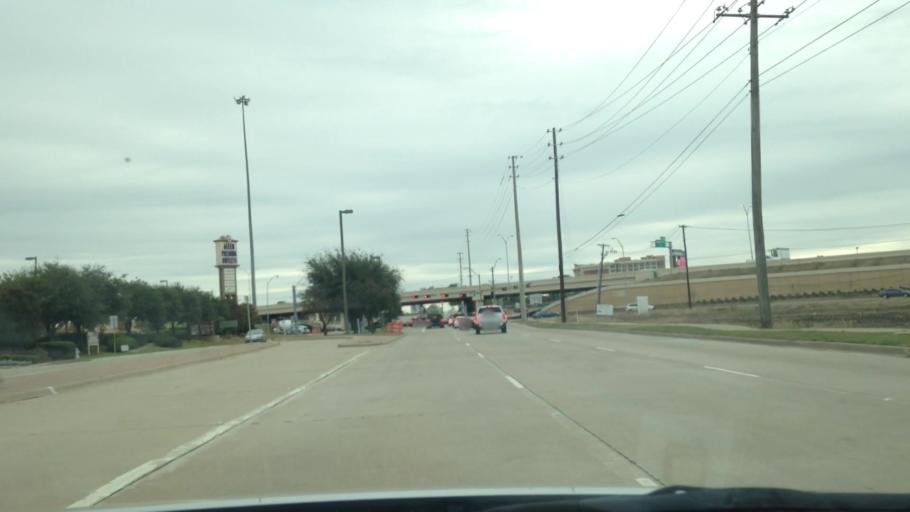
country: US
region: Texas
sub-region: Collin County
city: Allen
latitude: 33.1298
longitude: -96.6624
